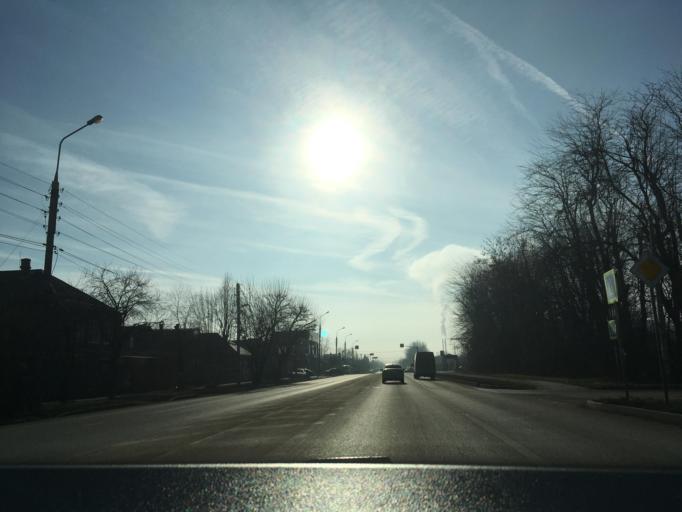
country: RU
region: Krasnodarskiy
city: Krasnodar
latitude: 45.1013
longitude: 39.0131
